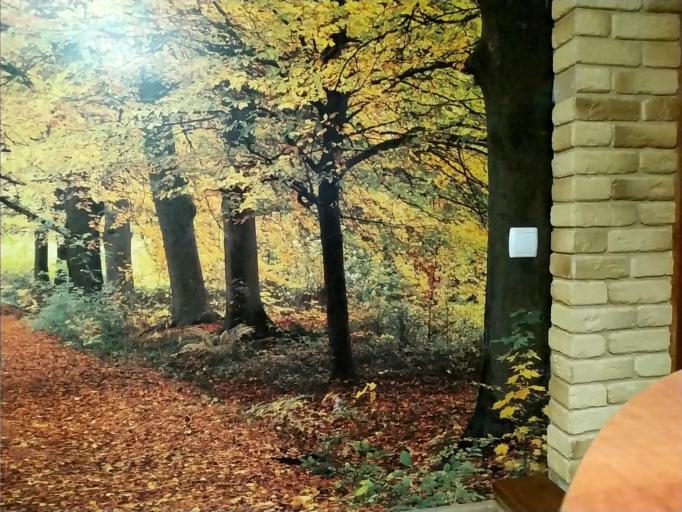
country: BY
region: Minsk
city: Il'ya
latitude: 54.4250
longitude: 27.5438
